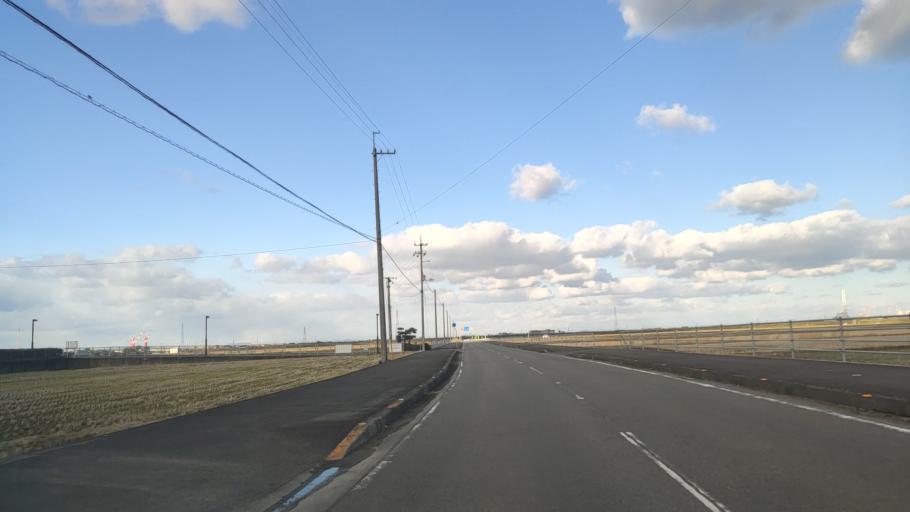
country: JP
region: Ehime
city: Saijo
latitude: 33.8998
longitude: 133.1352
